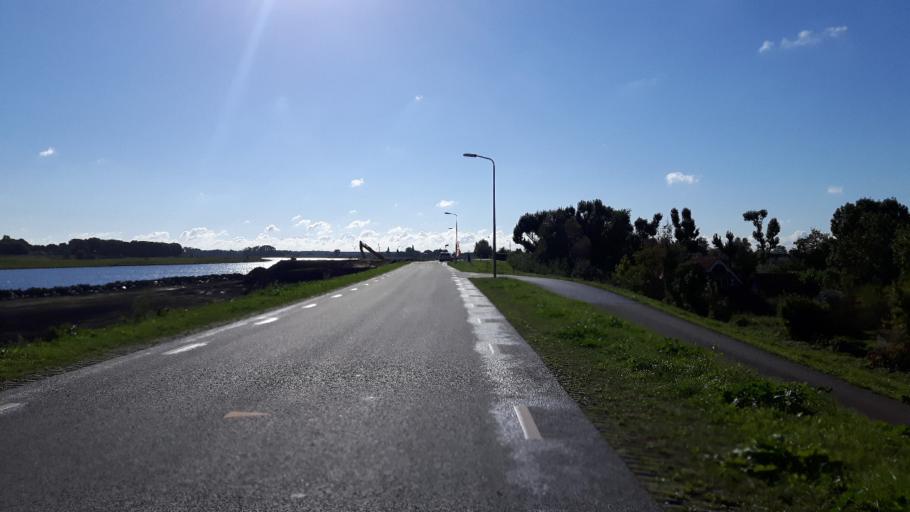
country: NL
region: Utrecht
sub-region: Gemeente Vianen
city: Vianen
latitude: 51.9799
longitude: 5.1419
